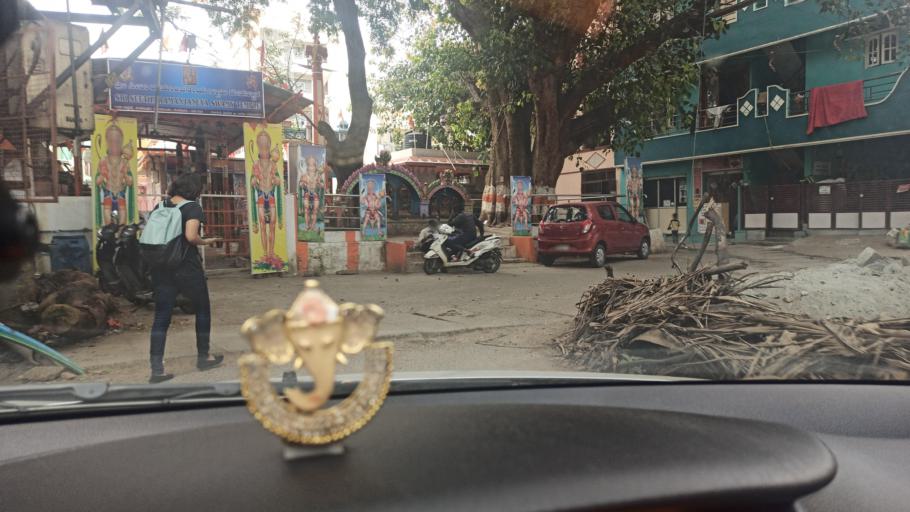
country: IN
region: Karnataka
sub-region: Bangalore Urban
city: Bangalore
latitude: 12.9186
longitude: 77.6338
